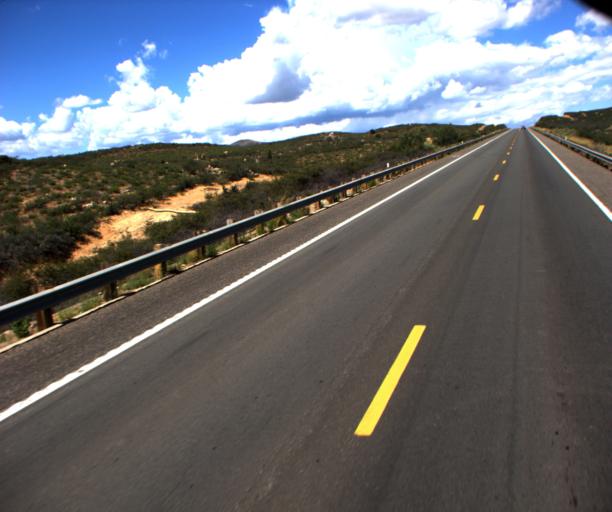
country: US
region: Arizona
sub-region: Yavapai County
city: Dewey-Humboldt
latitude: 34.5324
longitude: -112.1232
